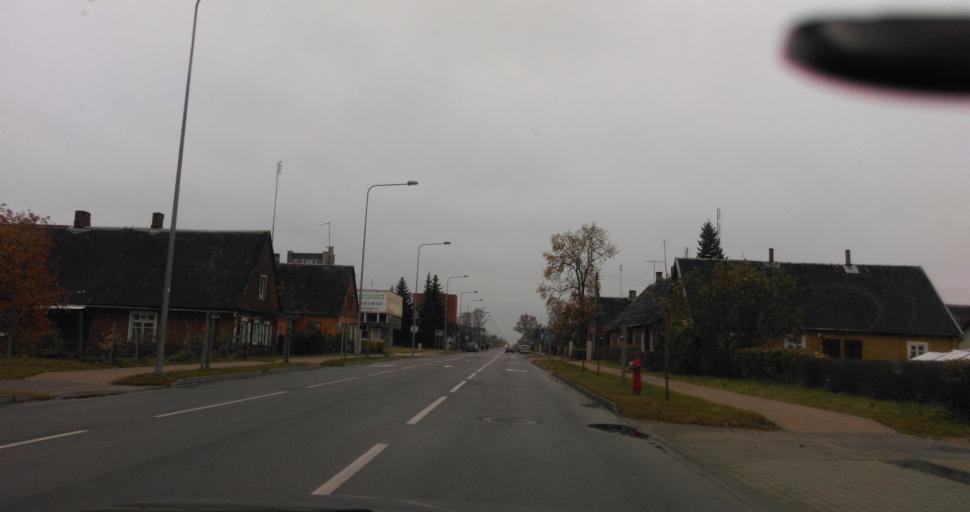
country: LT
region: Panevezys
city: Rokiskis
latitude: 55.9611
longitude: 25.5869
